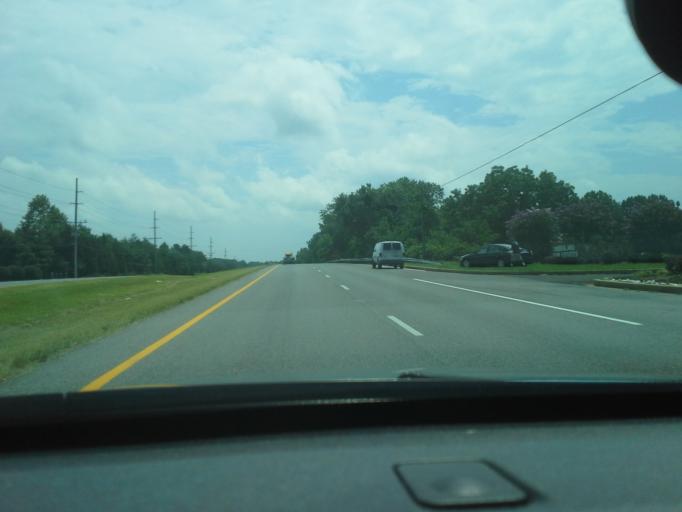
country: US
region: Maryland
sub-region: Calvert County
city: Owings
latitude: 38.6741
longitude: -76.6234
